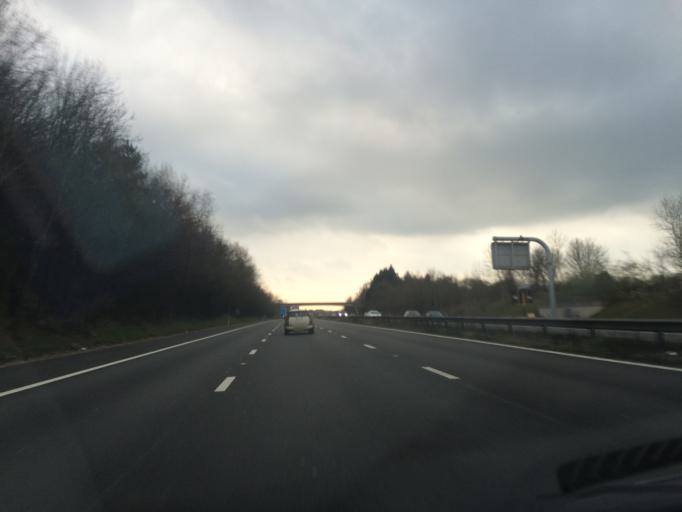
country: GB
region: England
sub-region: West Berkshire
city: Wickham
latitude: 51.4496
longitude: -1.4689
